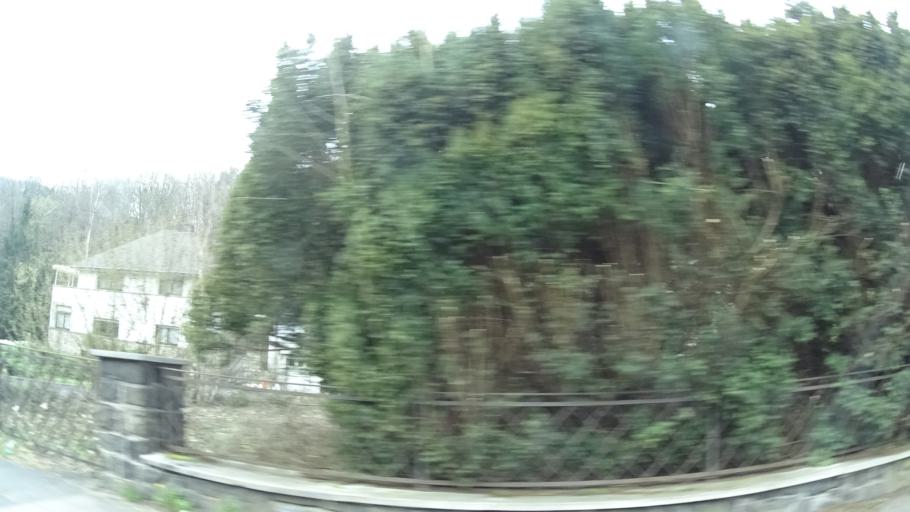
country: DE
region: Rheinland-Pfalz
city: Veitsrodt
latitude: 49.7344
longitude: 7.2827
